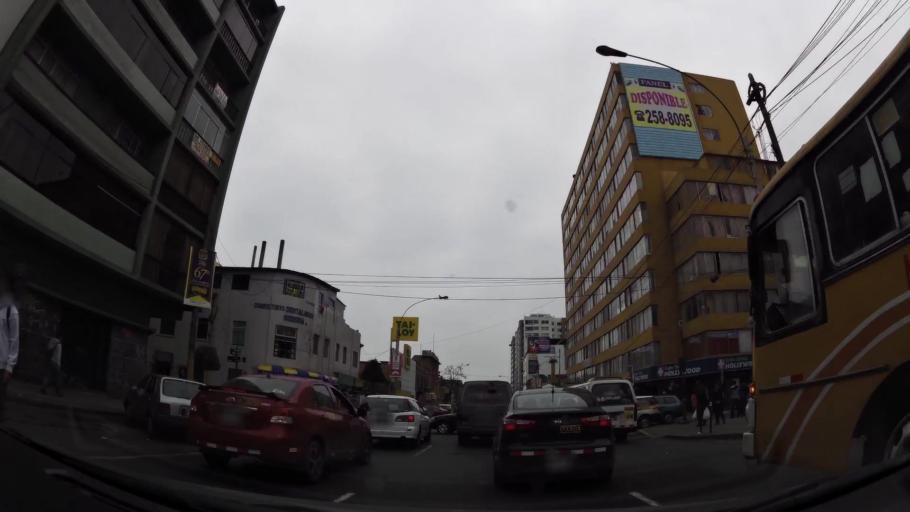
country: PE
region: Lima
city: Lima
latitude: -12.0546
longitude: -77.0436
